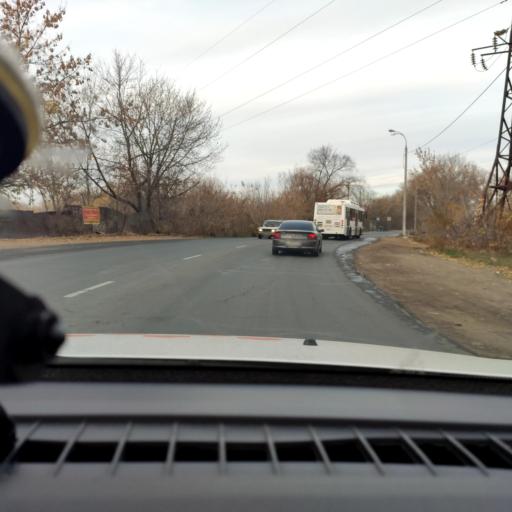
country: RU
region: Samara
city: Rozhdestveno
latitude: 53.1440
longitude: 50.0324
